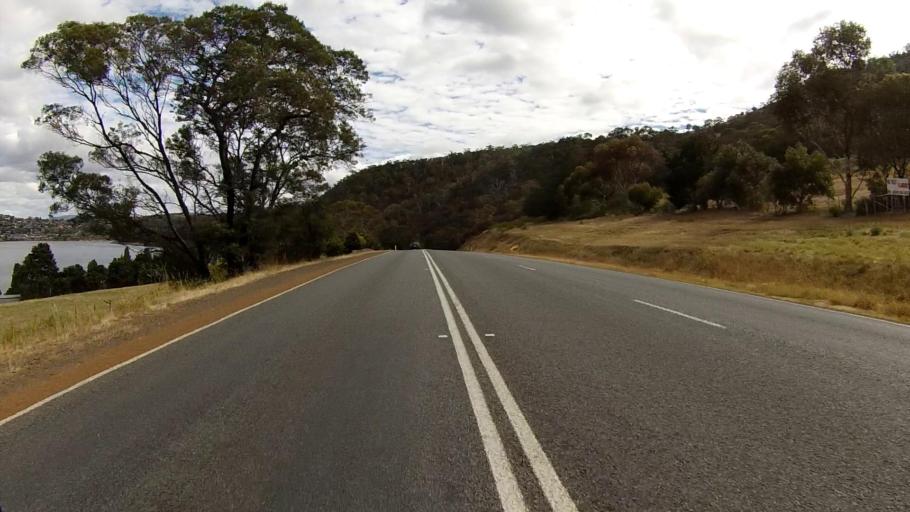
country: AU
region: Tasmania
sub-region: Brighton
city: Old Beach
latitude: -42.7933
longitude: 147.2928
